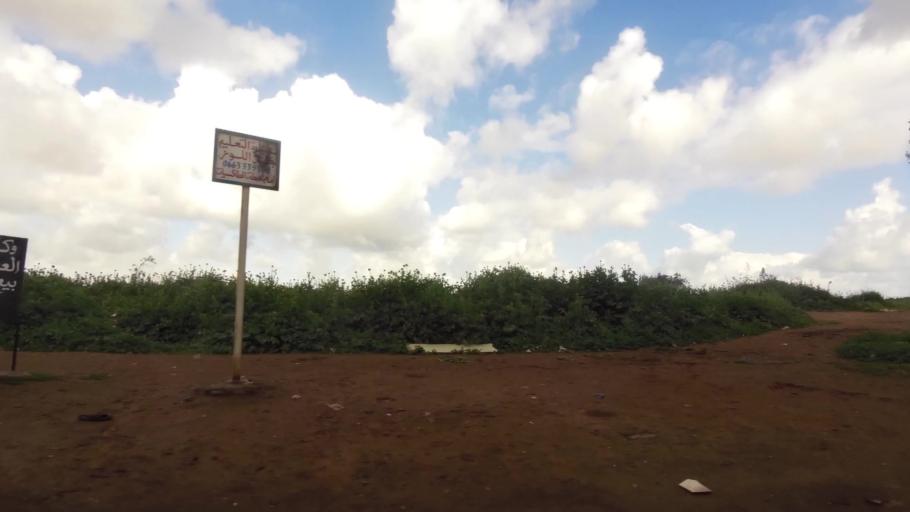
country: MA
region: Grand Casablanca
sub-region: Nouaceur
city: Bouskoura
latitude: 33.5374
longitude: -7.6974
